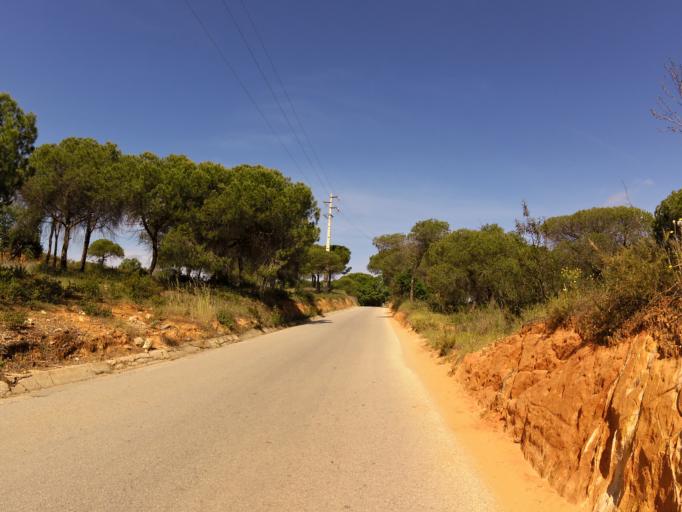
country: PT
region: Faro
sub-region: Loule
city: Almancil
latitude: 37.0678
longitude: -8.0103
